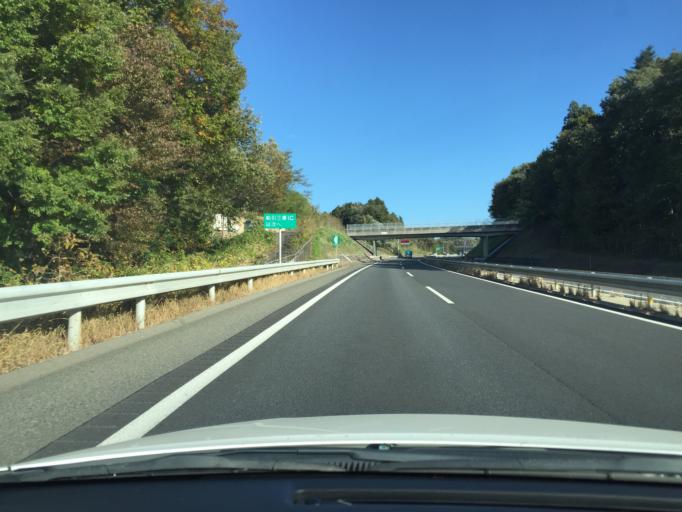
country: JP
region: Fukushima
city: Miharu
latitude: 37.4436
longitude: 140.4336
